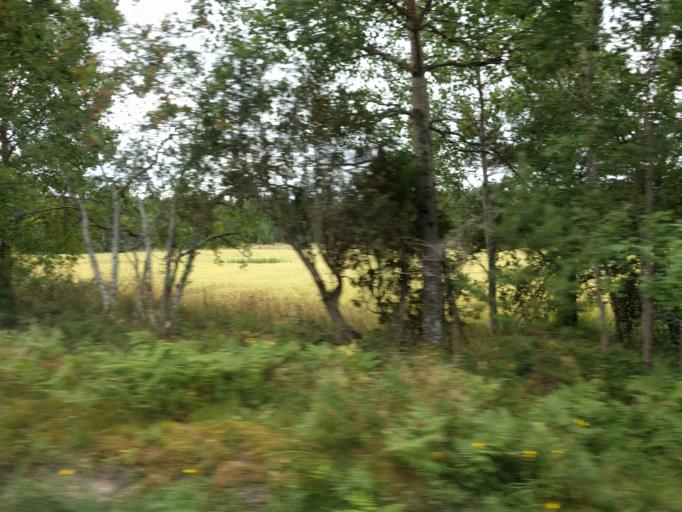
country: SE
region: Soedermanland
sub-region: Nykopings Kommun
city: Svalsta
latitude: 58.4968
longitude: 16.8827
